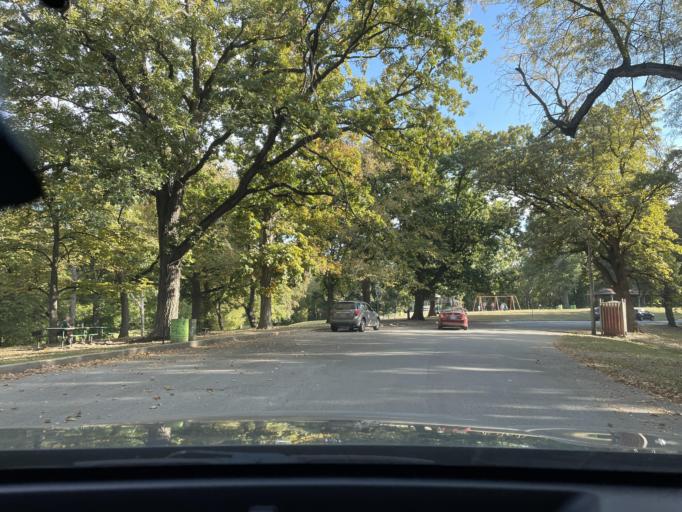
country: US
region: Missouri
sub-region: Buchanan County
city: Saint Joseph
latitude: 39.7985
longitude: -94.8516
